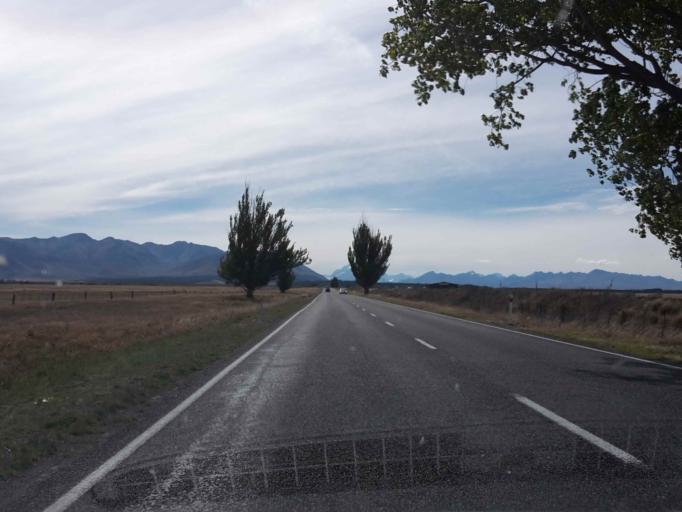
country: NZ
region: Canterbury
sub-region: Timaru District
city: Pleasant Point
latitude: -44.2486
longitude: 170.1164
